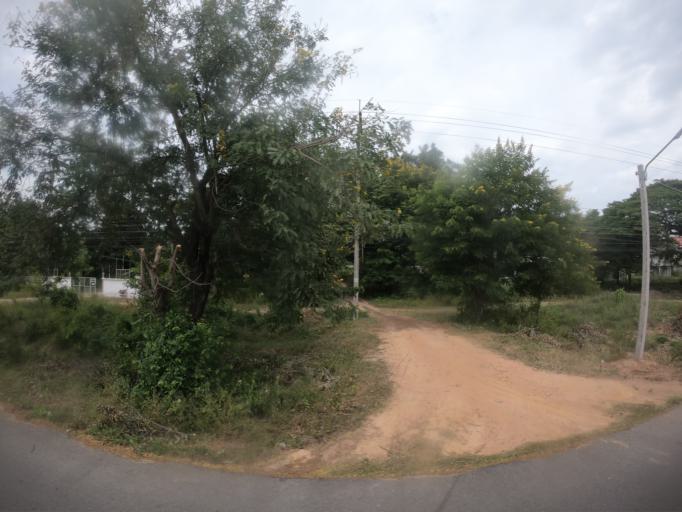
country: TH
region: Maha Sarakham
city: Maha Sarakham
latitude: 16.1466
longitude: 103.4096
